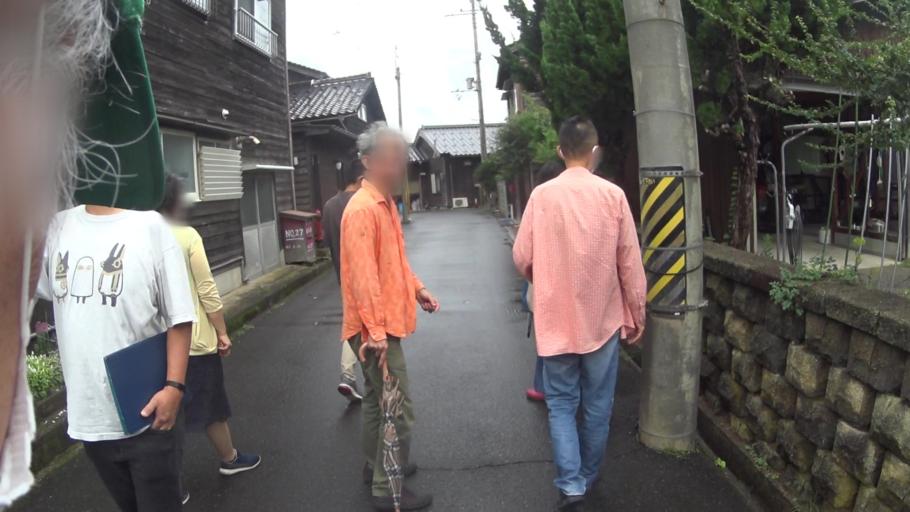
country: JP
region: Hyogo
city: Toyooka
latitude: 35.6605
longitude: 134.9637
